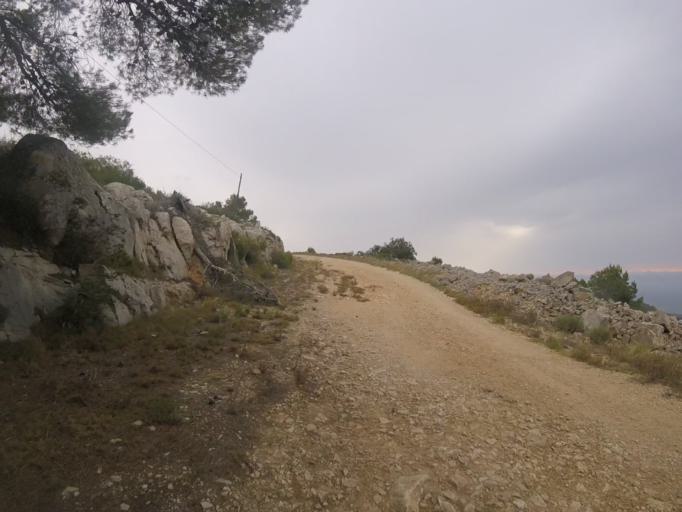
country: ES
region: Valencia
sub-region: Provincia de Castello
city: Alcoceber
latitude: 40.2788
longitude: 0.2829
